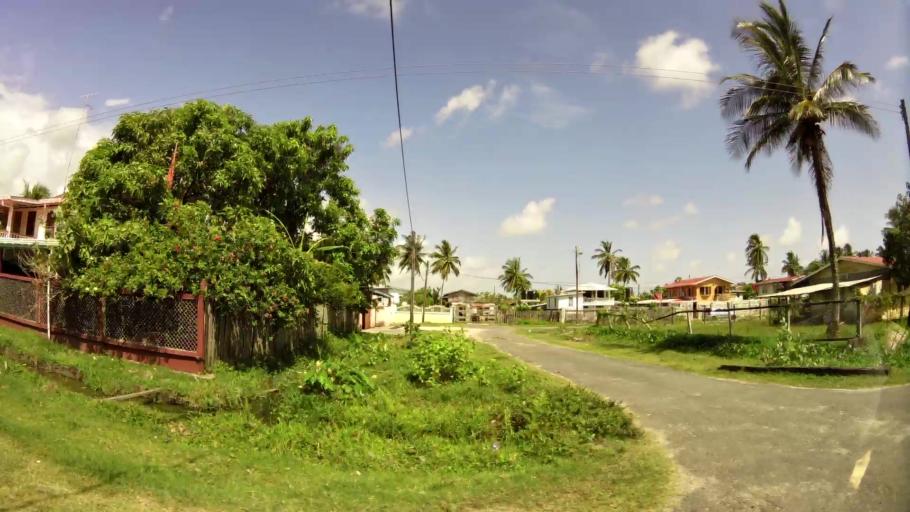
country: GY
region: Demerara-Mahaica
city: Mahaica Village
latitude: 6.7564
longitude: -57.9943
